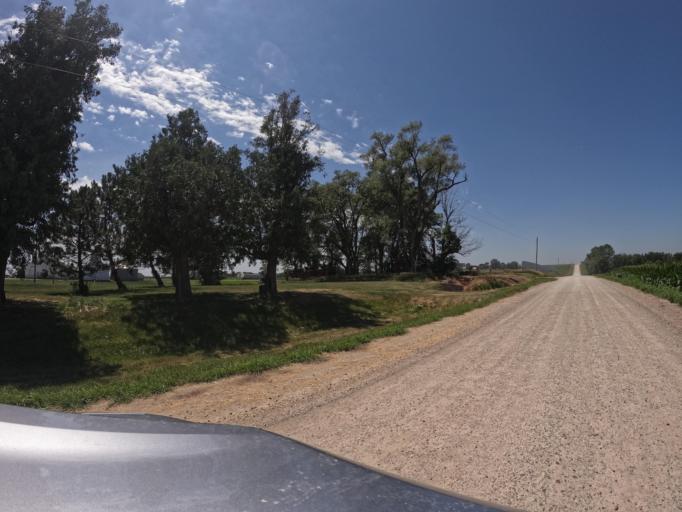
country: US
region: Iowa
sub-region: Poweshiek County
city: Montezuma
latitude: 41.4666
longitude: -92.3663
